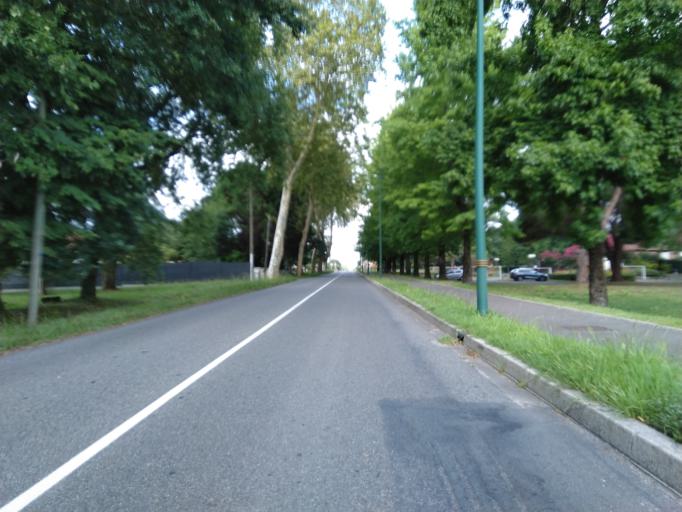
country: FR
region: Aquitaine
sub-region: Departement des Landes
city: Mees
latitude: 43.7298
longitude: -1.0915
